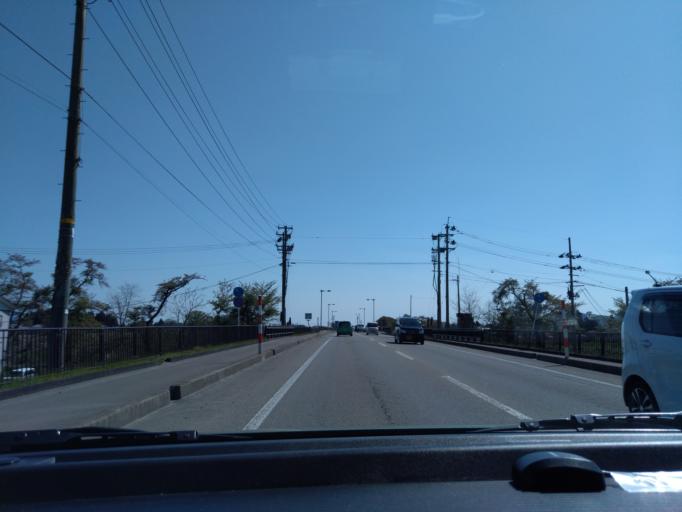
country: JP
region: Akita
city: Kakunodatemachi
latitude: 39.5816
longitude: 140.5686
